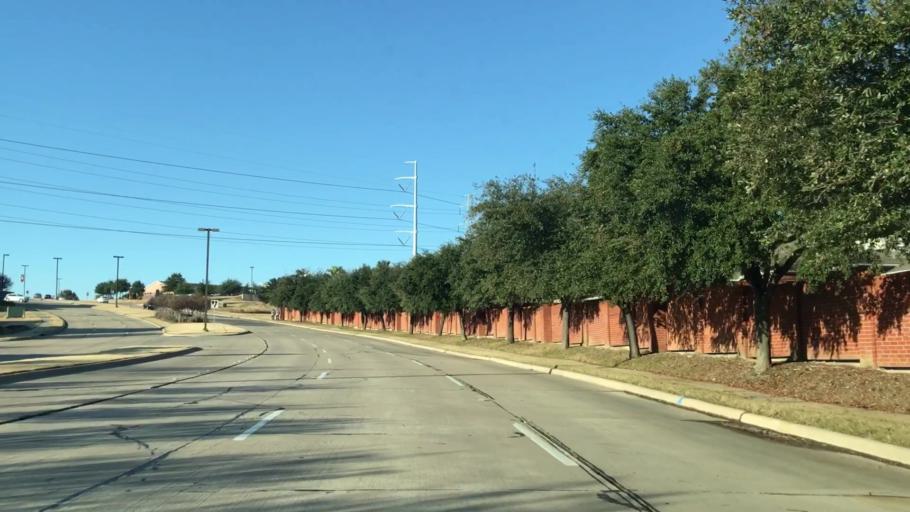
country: US
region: Texas
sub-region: Dallas County
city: Coppell
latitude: 32.9273
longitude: -96.9630
